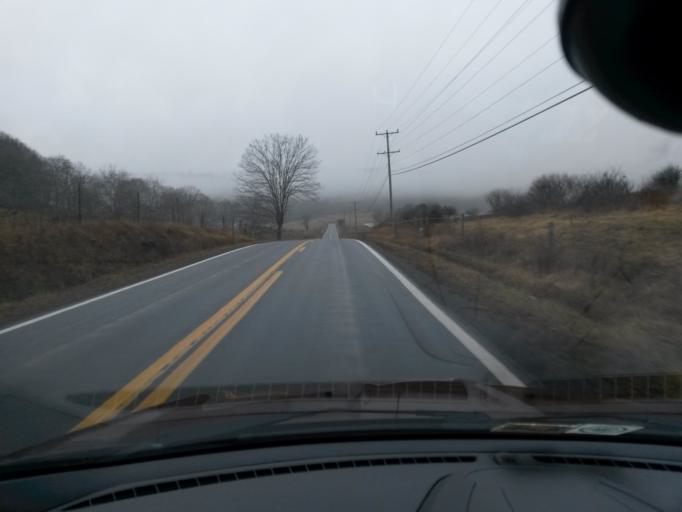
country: US
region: West Virginia
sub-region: Greenbrier County
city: Lewisburg
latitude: 37.8736
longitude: -80.5200
